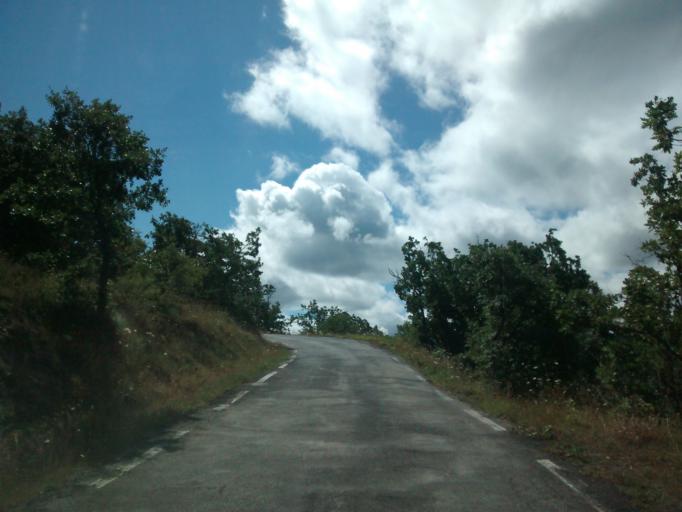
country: ES
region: Castille and Leon
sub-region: Provincia de Palencia
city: Berzosilla
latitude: 42.8687
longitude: -4.0576
